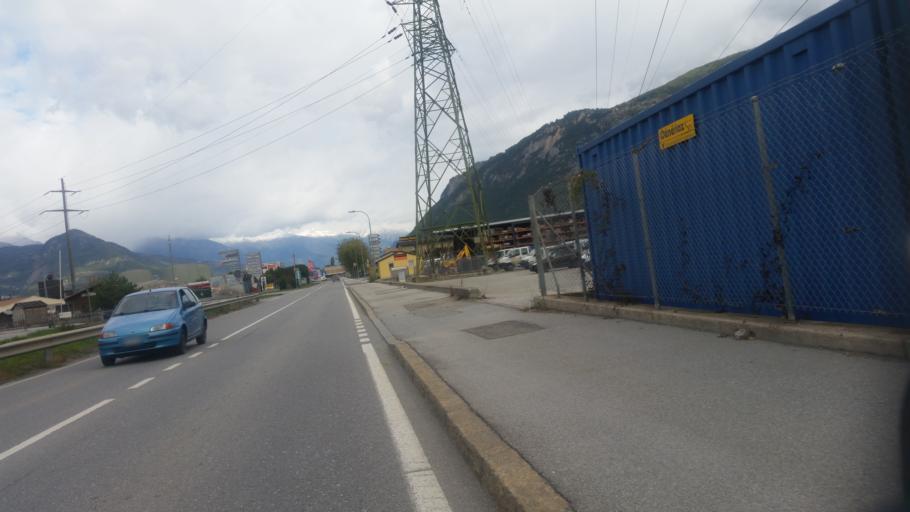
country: CH
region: Valais
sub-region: Sion District
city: Sitten
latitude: 46.2219
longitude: 7.3660
